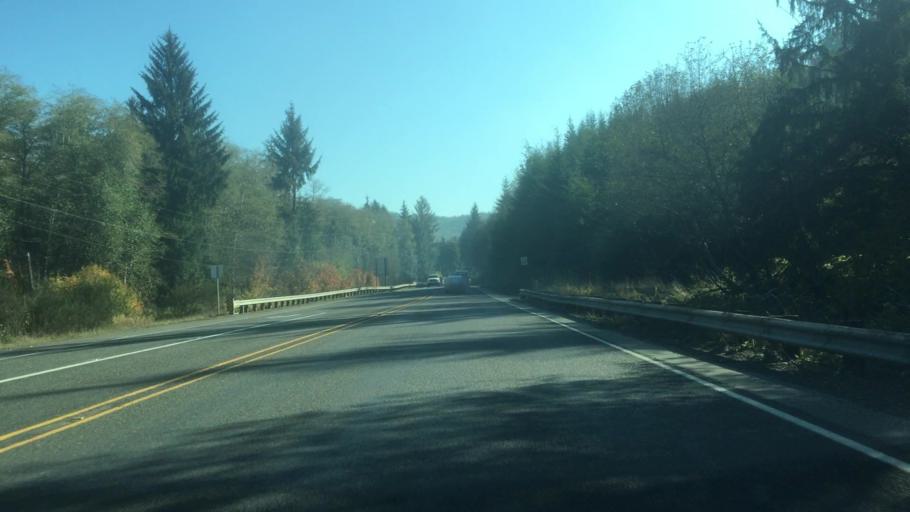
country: US
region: Washington
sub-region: Grays Harbor County
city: Central Park
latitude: 46.9174
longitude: -123.7189
